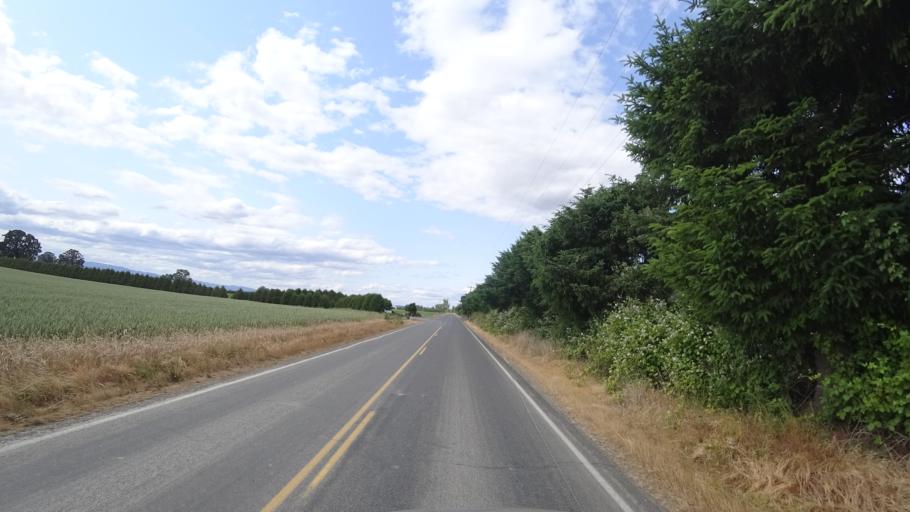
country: US
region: Washington
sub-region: Clark County
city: Felida
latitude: 45.6562
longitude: -122.7793
